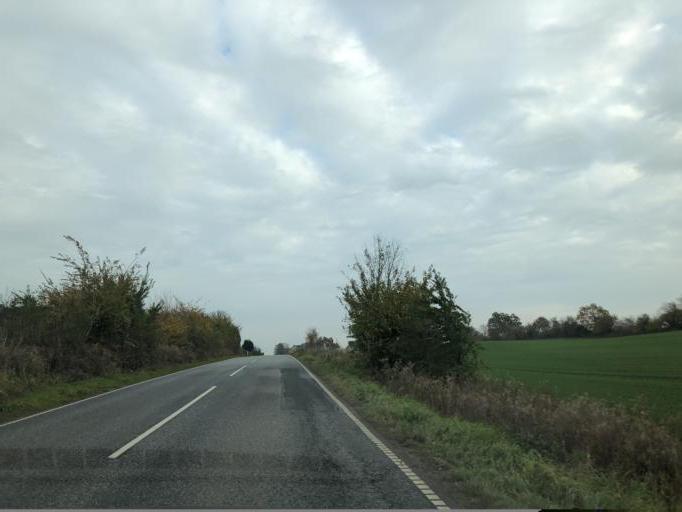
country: DK
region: Central Jutland
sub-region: Hedensted Kommune
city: Hedensted
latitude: 55.7355
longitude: 9.7580
